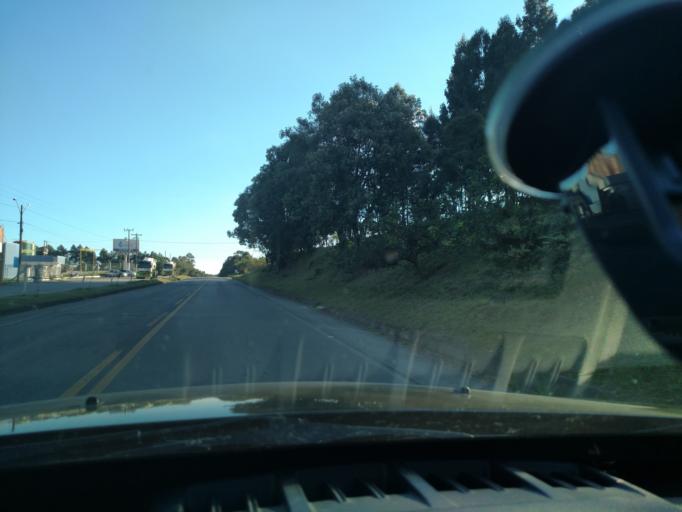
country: BR
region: Santa Catarina
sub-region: Otacilio Costa
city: Otacilio Costa
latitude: -27.5974
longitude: -50.1709
